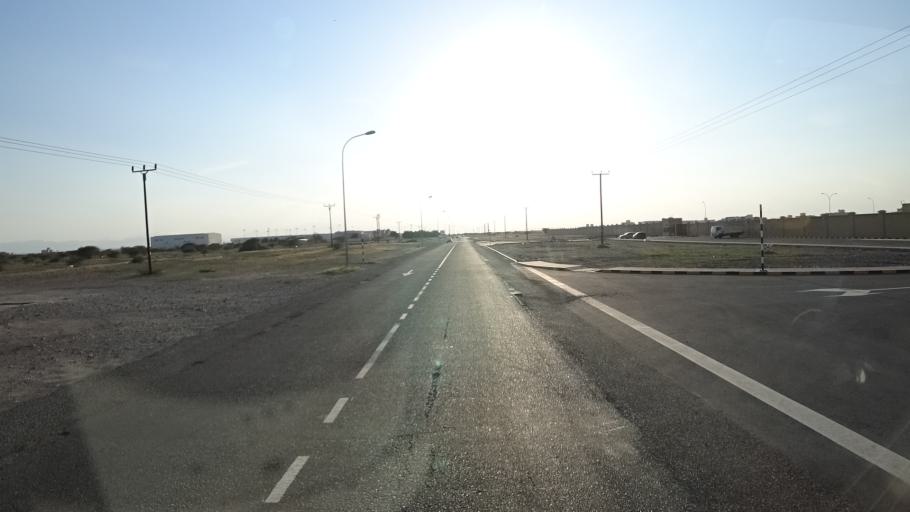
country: OM
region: Al Batinah
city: Al Khaburah
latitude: 23.9494
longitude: 57.0555
